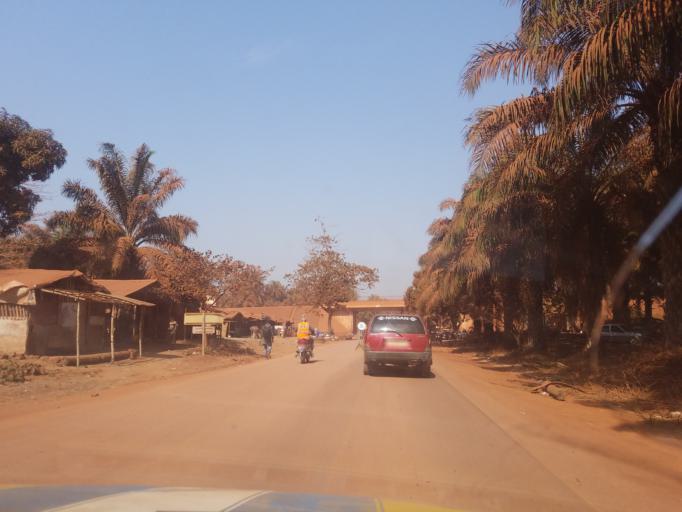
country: GN
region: Boke
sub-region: Boke Prefecture
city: Sangueya
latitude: 10.8106
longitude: -14.3849
